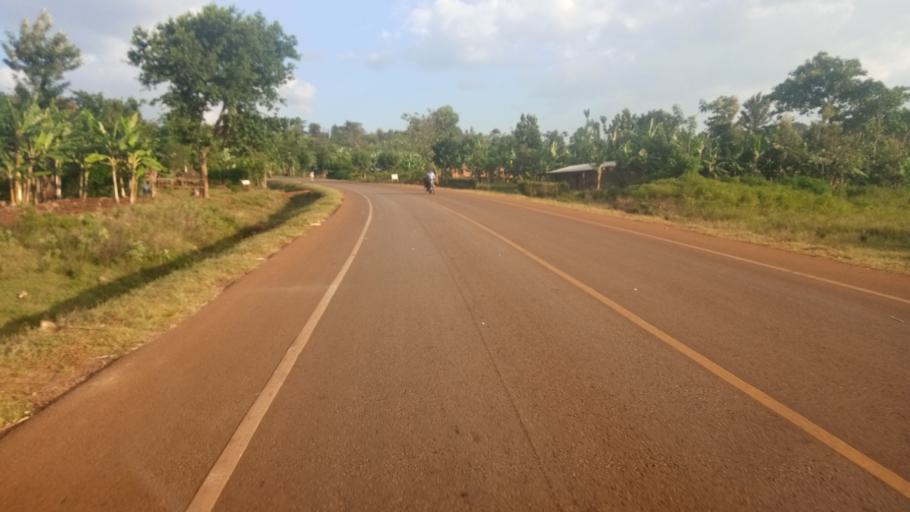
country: UG
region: Eastern Region
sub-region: Sironko District
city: Sironko
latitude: 1.3291
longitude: 34.3258
